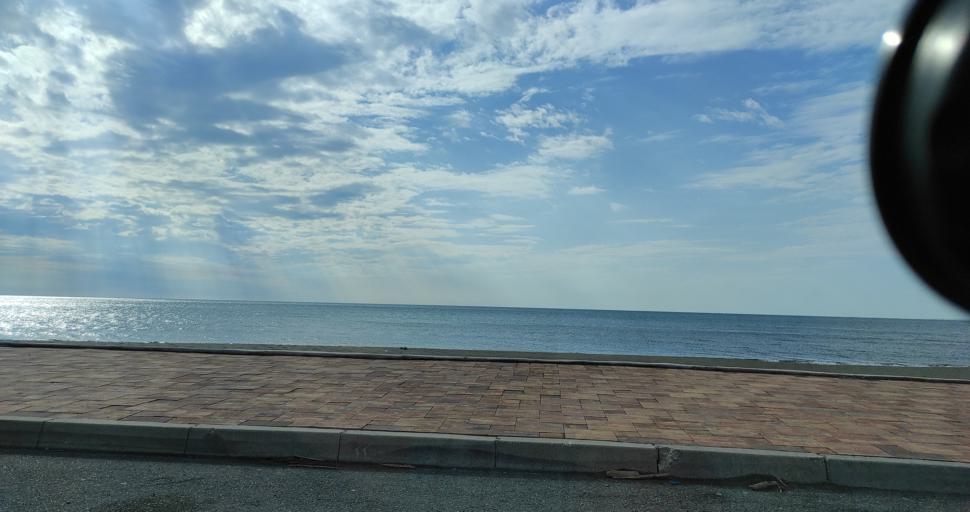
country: AL
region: Lezhe
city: Shengjin
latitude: 41.7979
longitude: 19.6014
